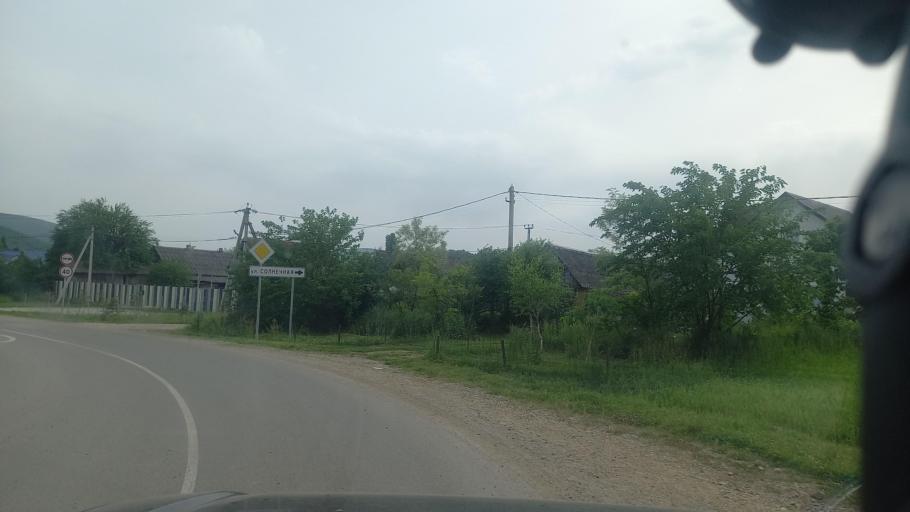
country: RU
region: Krasnodarskiy
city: Goryachiy Klyuch
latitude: 44.6081
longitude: 39.0235
